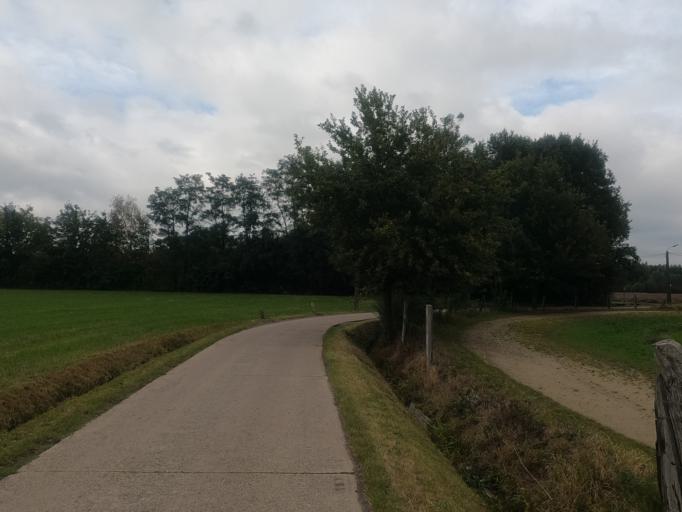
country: BE
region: Flanders
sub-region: Provincie Antwerpen
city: Nijlen
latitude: 51.1461
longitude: 4.6554
